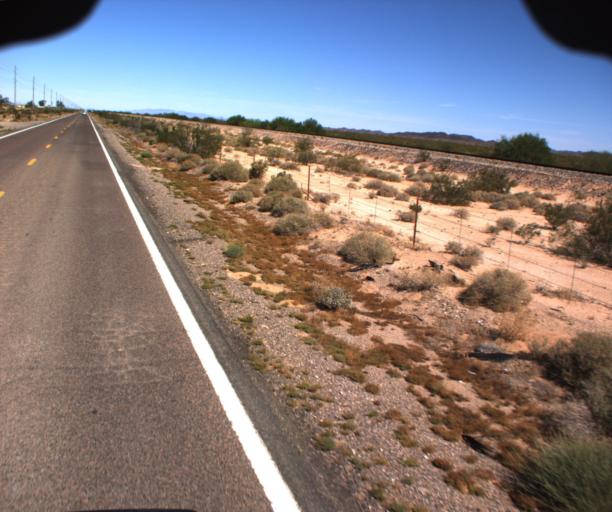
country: US
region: Arizona
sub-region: La Paz County
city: Salome
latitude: 33.8591
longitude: -113.9155
